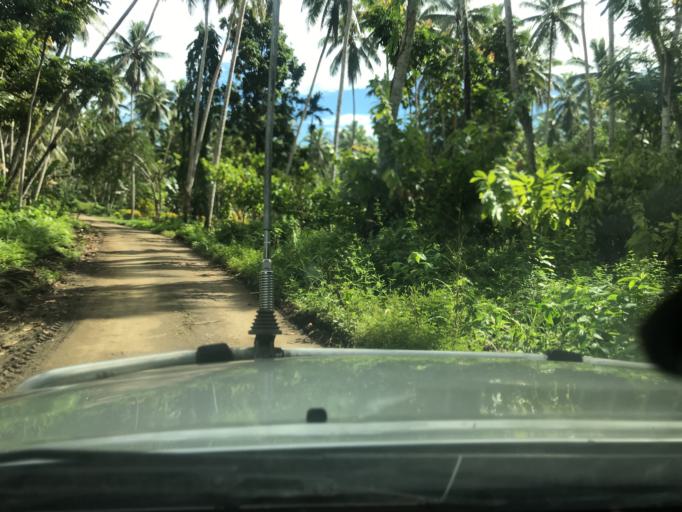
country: SB
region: Malaita
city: Auki
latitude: -8.9319
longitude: 160.7684
